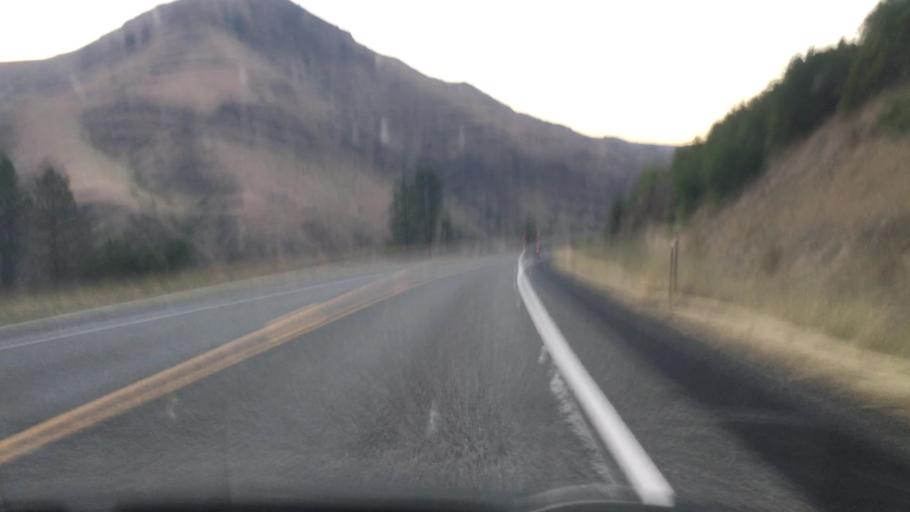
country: US
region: Idaho
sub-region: Idaho County
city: Grangeville
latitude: 45.6946
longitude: -116.3146
